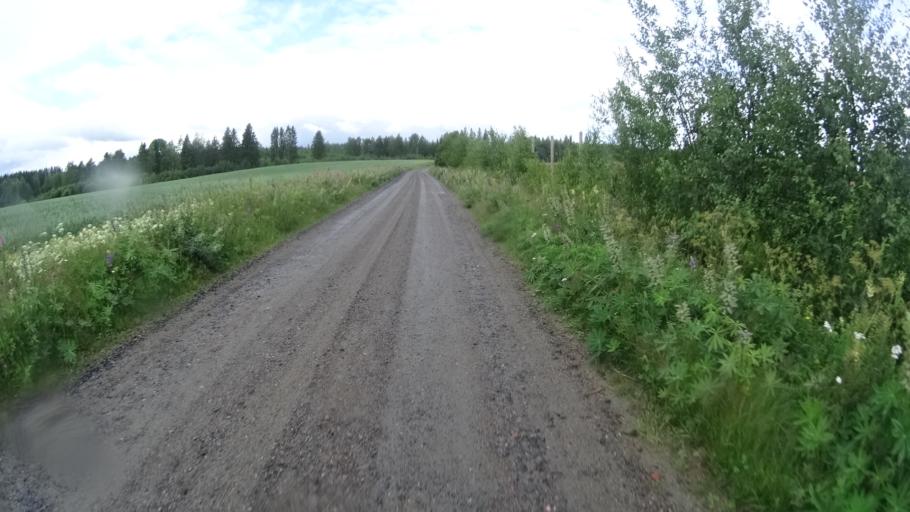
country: FI
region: Uusimaa
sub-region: Helsinki
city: Karkkila
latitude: 60.5851
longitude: 24.3408
